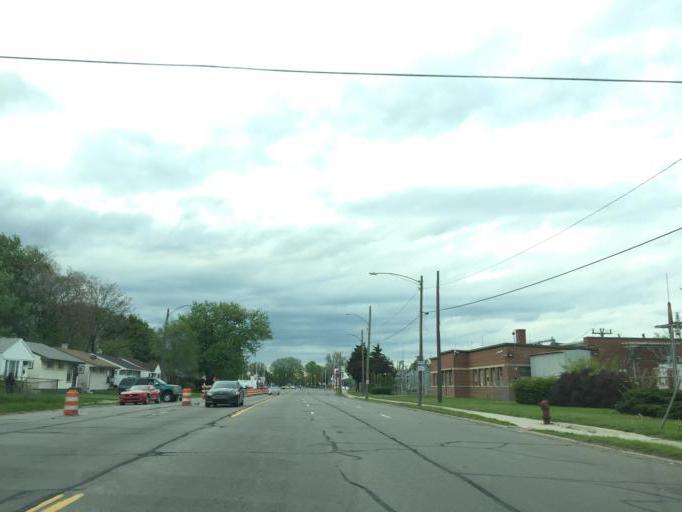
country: US
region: Michigan
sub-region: Wayne County
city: Dearborn Heights
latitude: 42.3837
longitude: -83.2367
